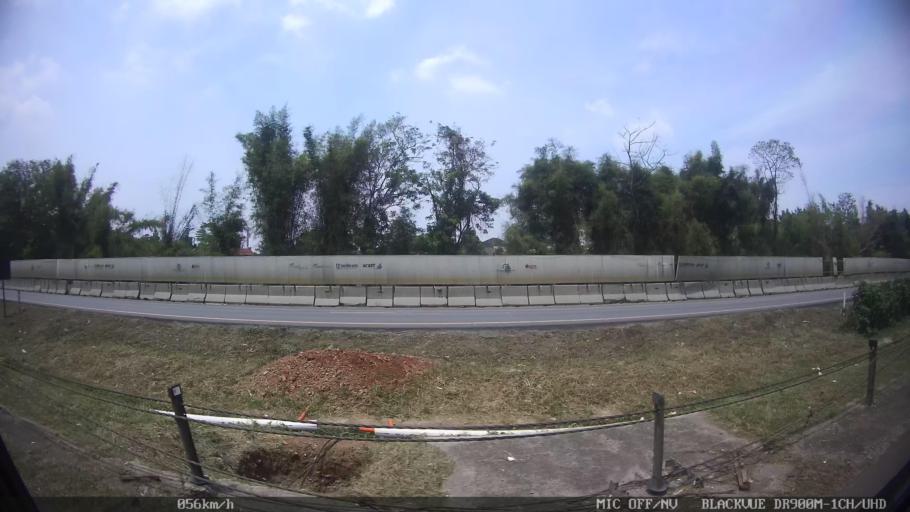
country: ID
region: Banten
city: Serang
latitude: -6.1252
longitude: 106.1913
